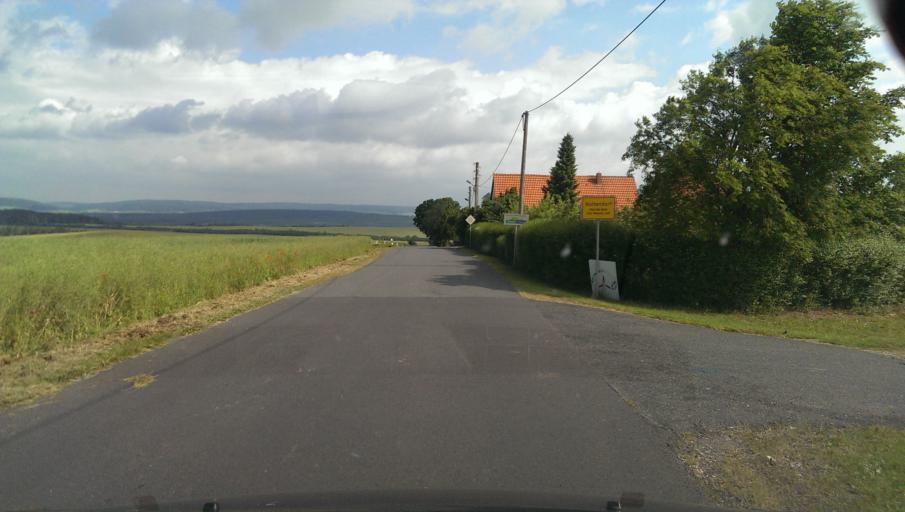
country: DE
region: Thuringia
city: Rittersdorf
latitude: 50.8294
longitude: 11.2397
